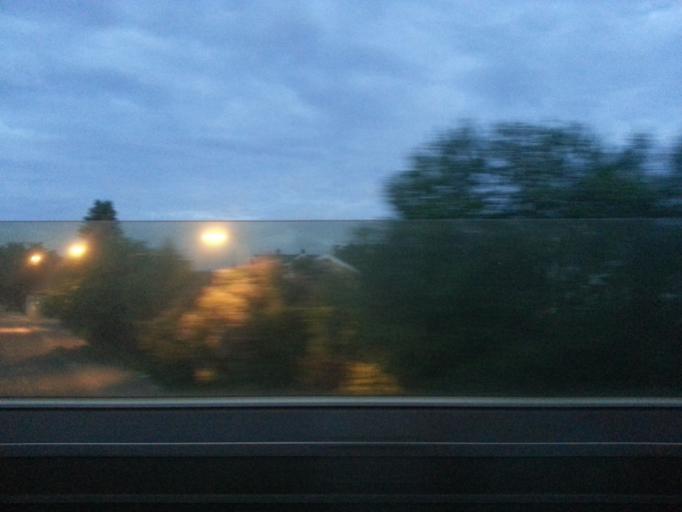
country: NO
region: Akershus
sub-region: Skedsmo
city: Lillestrom
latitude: 59.9555
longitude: 11.0541
